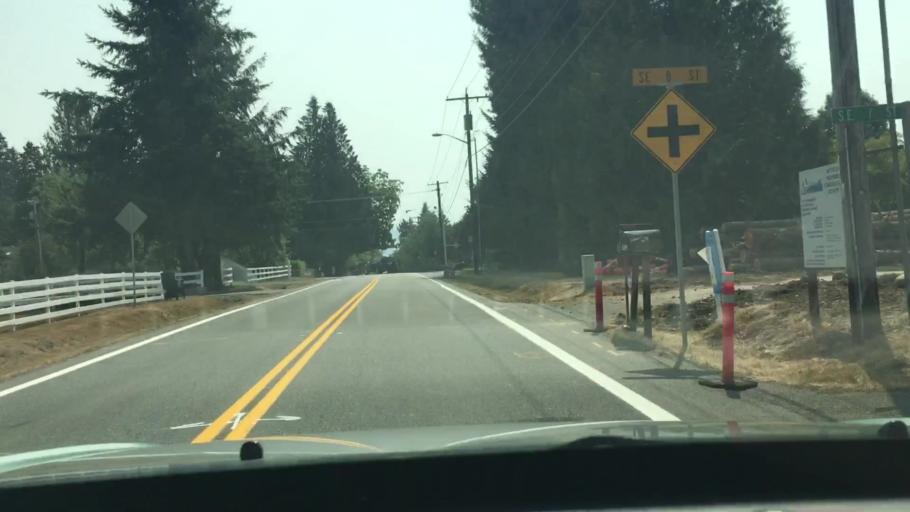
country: US
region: Washington
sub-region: King County
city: City of Sammamish
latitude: 47.6032
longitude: -122.0572
